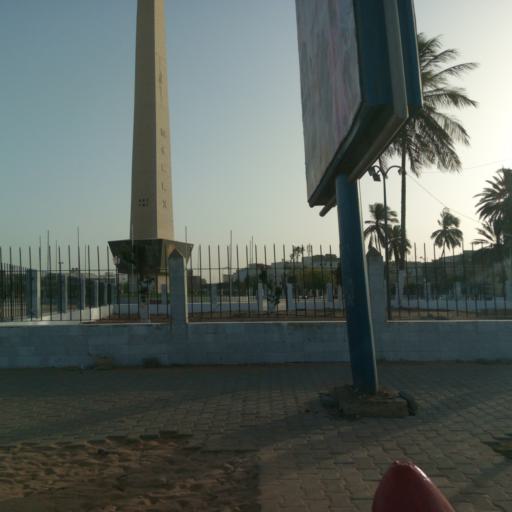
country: SN
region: Dakar
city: Dakar
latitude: 14.6937
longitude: -17.4487
